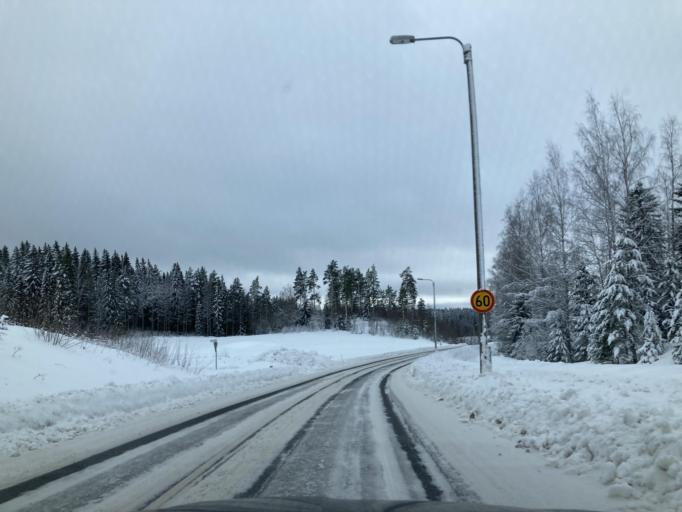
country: FI
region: Central Finland
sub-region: Jaemsae
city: Jaemsae
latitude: 61.8756
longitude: 25.2739
